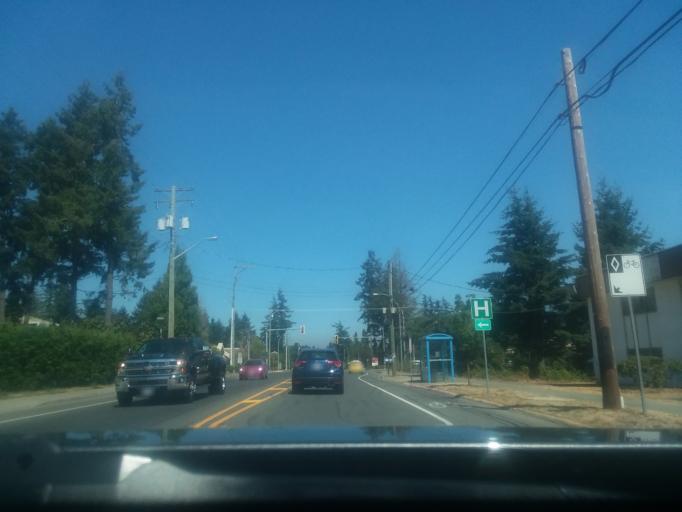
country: CA
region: British Columbia
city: Courtenay
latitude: 49.6874
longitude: -124.9349
